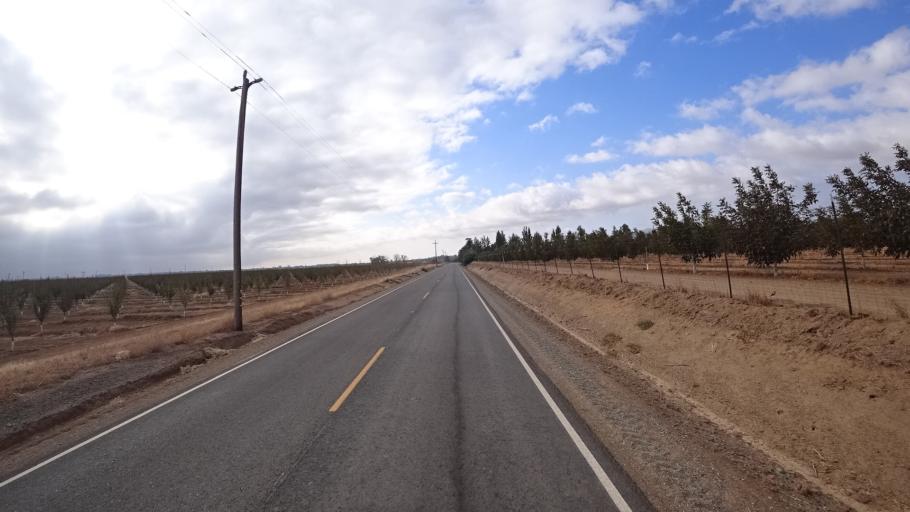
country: US
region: California
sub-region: Yolo County
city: Esparto
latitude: 38.7231
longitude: -122.0465
